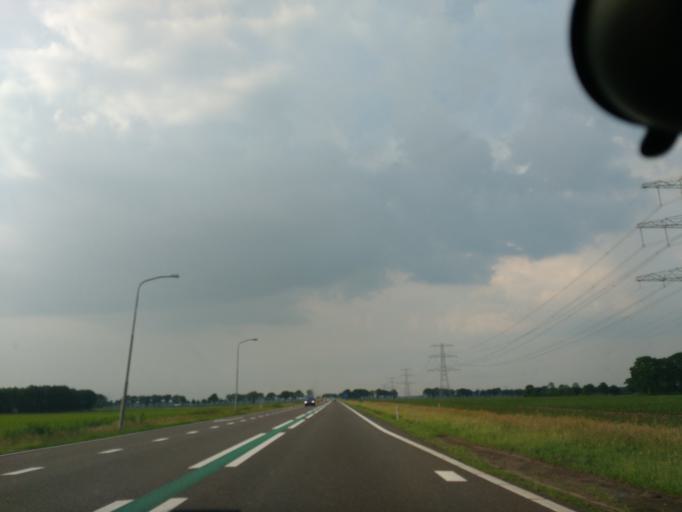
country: NL
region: Drenthe
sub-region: Gemeente Coevorden
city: Sleen
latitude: 52.7774
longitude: 6.8452
